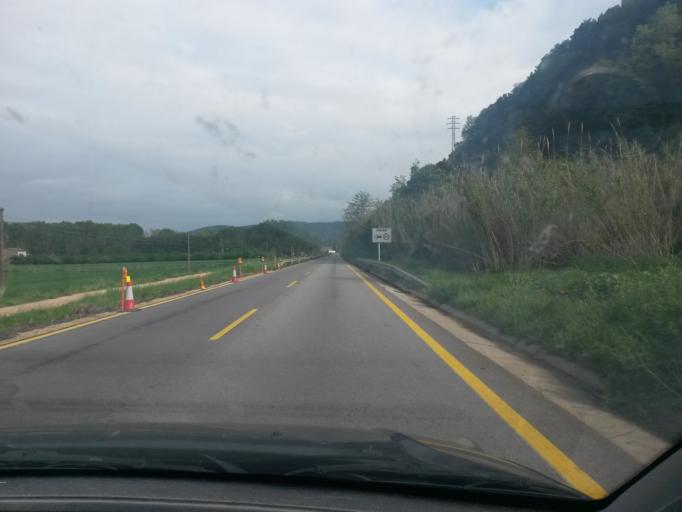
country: ES
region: Catalonia
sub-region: Provincia de Girona
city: Sant Gregori
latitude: 41.9734
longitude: 2.7141
